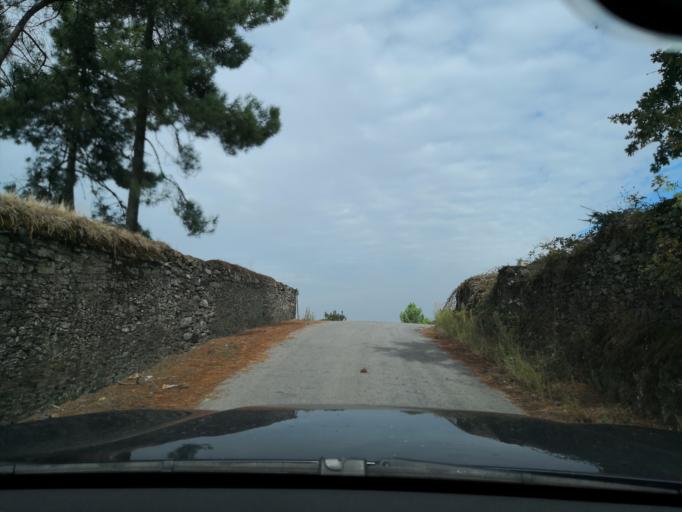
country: PT
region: Vila Real
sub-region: Peso da Regua
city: Peso da Regua
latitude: 41.2039
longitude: -7.7010
